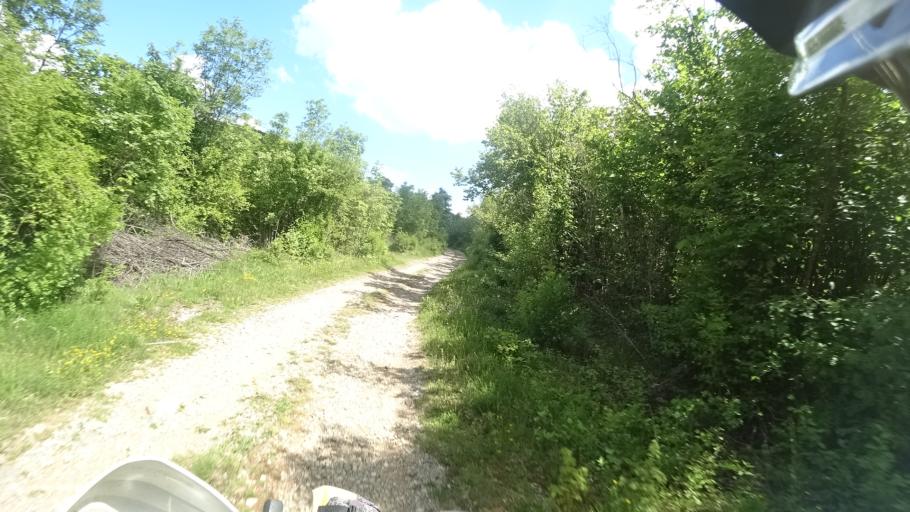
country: HR
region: Zadarska
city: Gracac
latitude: 44.2707
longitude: 15.9259
